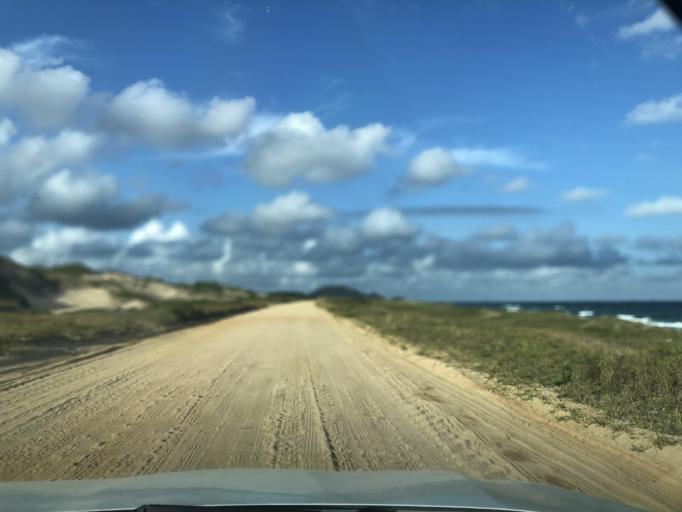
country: BR
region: Santa Catarina
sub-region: Sao Francisco Do Sul
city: Sao Francisco do Sul
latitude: -26.2575
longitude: -48.5172
